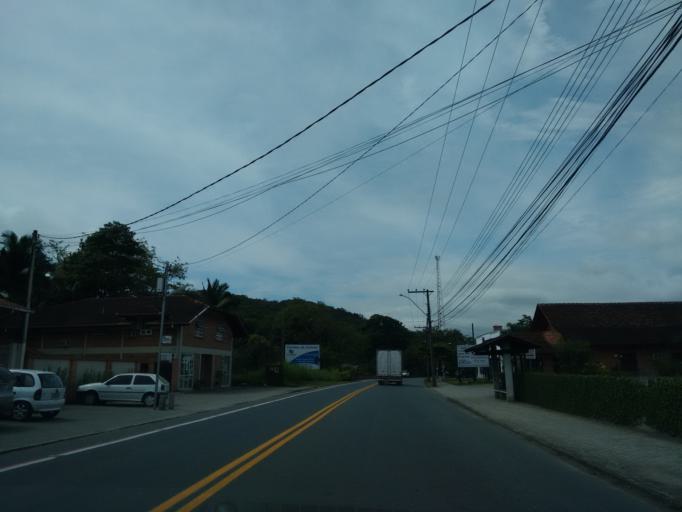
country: BR
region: Santa Catarina
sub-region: Pomerode
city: Pomerode
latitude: -26.7112
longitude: -49.1642
